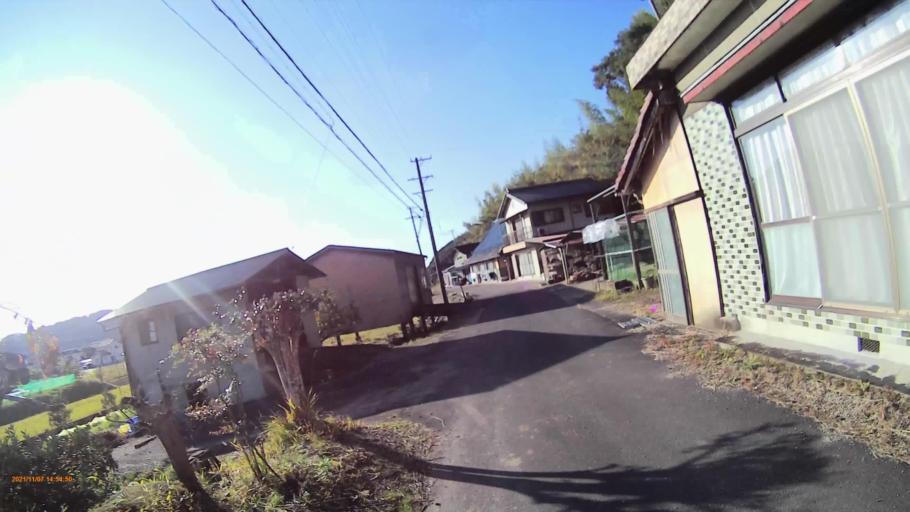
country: JP
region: Gifu
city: Mitake
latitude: 35.4290
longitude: 137.1560
